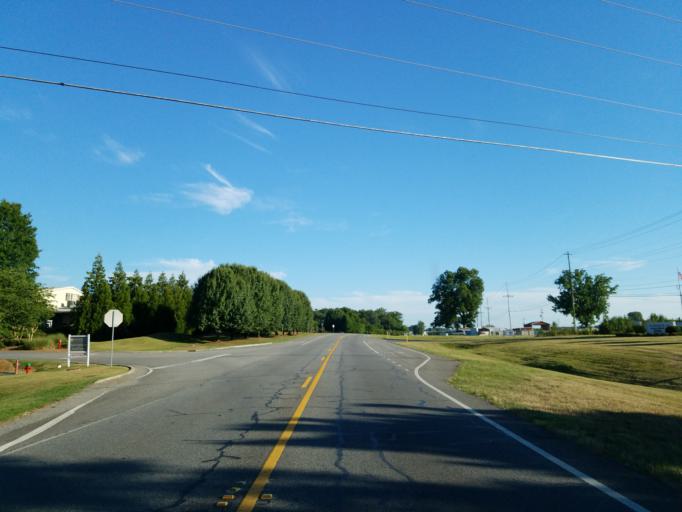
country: US
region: Georgia
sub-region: Gordon County
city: Calhoun
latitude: 34.4592
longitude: -84.9344
